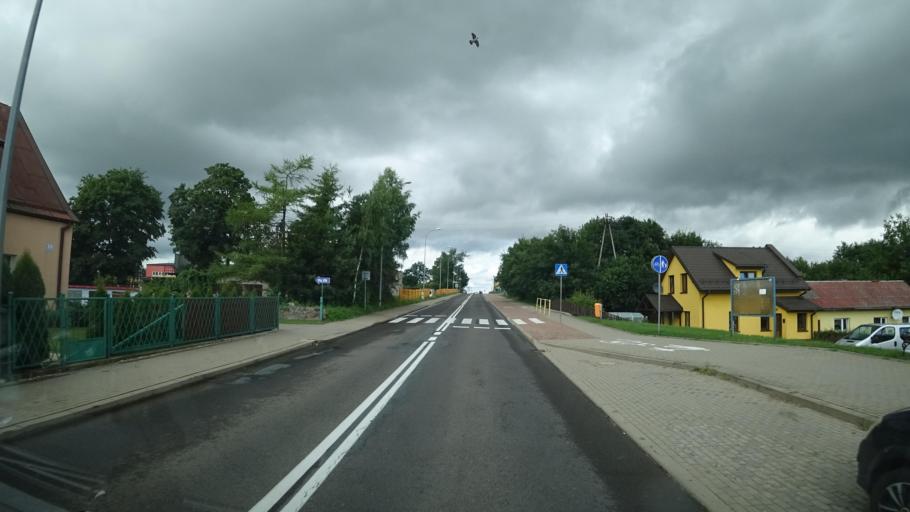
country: PL
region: Warmian-Masurian Voivodeship
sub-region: Powiat olecki
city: Kowale Oleckie
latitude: 54.1642
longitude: 22.4157
